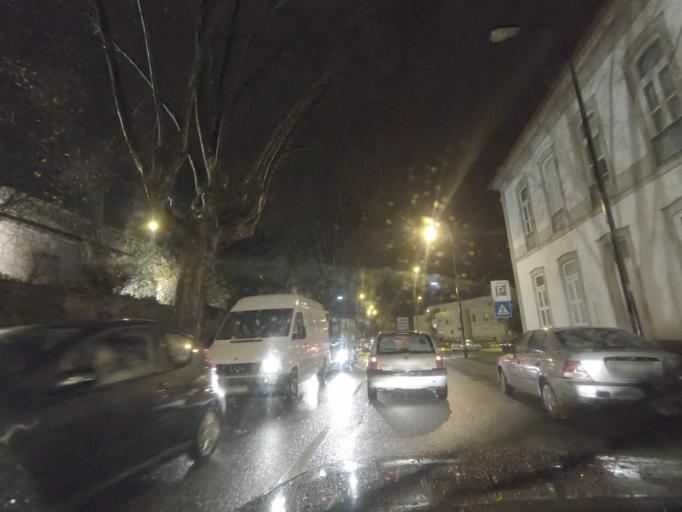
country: PT
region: Vila Real
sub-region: Vila Real
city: Vila Real
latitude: 41.3006
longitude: -7.7412
